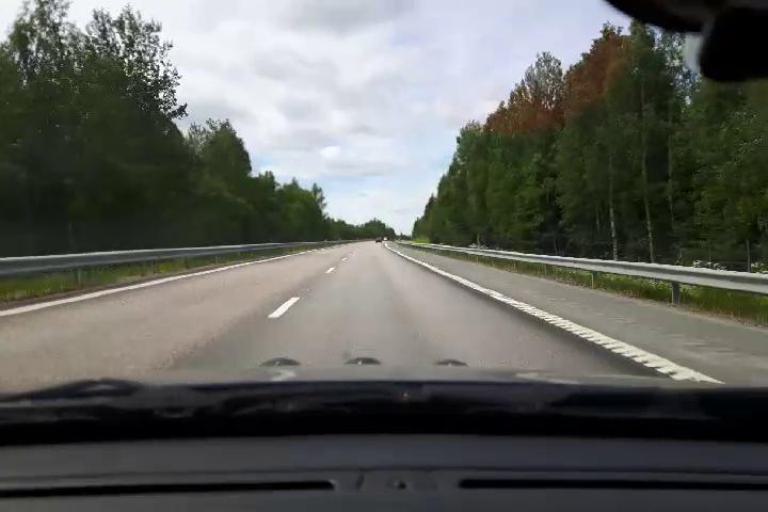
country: SE
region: Uppsala
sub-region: Alvkarleby Kommun
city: AElvkarleby
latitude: 60.4764
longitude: 17.3762
